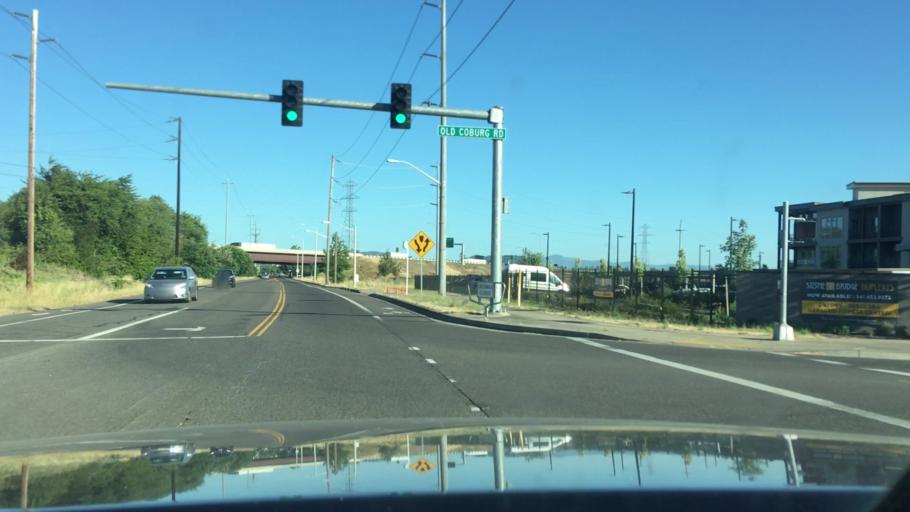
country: US
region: Oregon
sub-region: Lane County
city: Coburg
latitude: 44.0910
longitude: -123.0488
